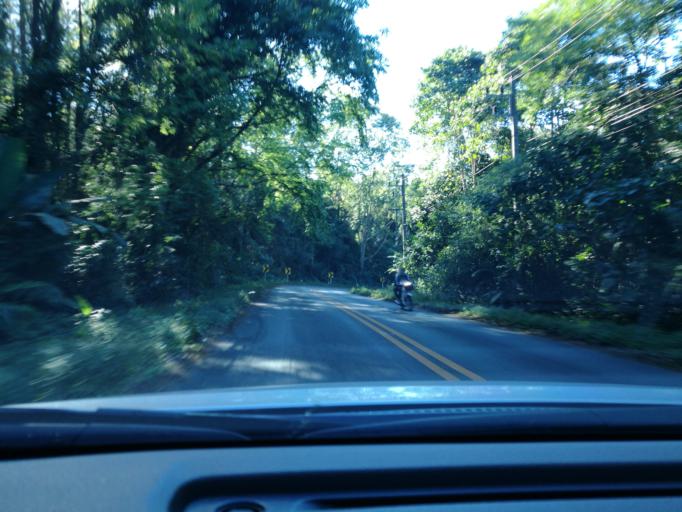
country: TH
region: Phitsanulok
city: Nakhon Thai
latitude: 16.9971
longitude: 101.0130
